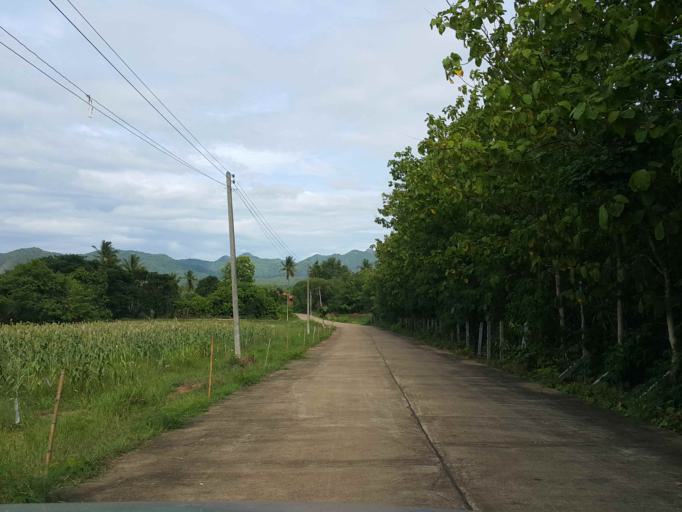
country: TH
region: Sukhothai
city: Thung Saliam
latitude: 17.2275
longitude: 99.5281
